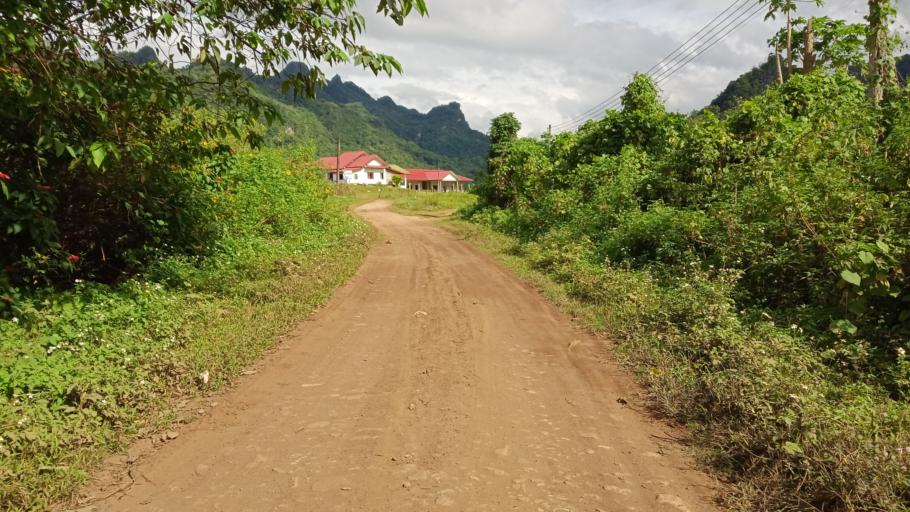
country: LA
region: Xiangkhoang
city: Phonsavan
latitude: 19.1044
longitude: 102.9317
